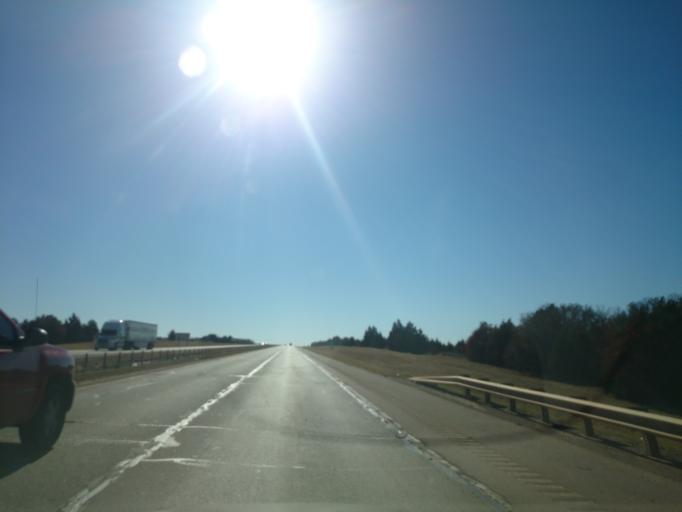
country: US
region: Oklahoma
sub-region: Logan County
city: Guthrie
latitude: 35.8557
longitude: -97.3944
